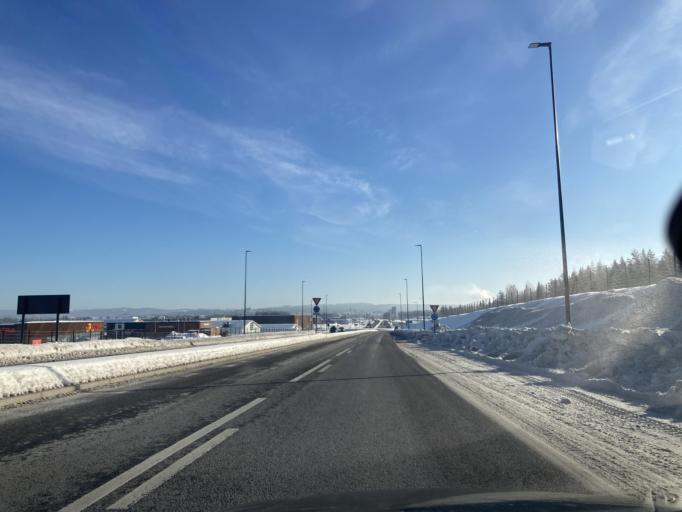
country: NO
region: Hedmark
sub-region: Elverum
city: Elverum
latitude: 60.8871
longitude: 11.5113
